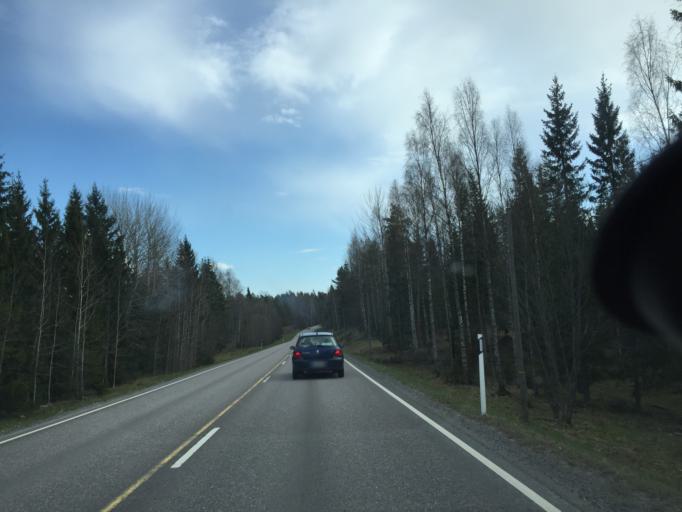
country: FI
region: Uusimaa
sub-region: Raaseporin
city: Ekenaes
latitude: 60.0259
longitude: 23.3719
